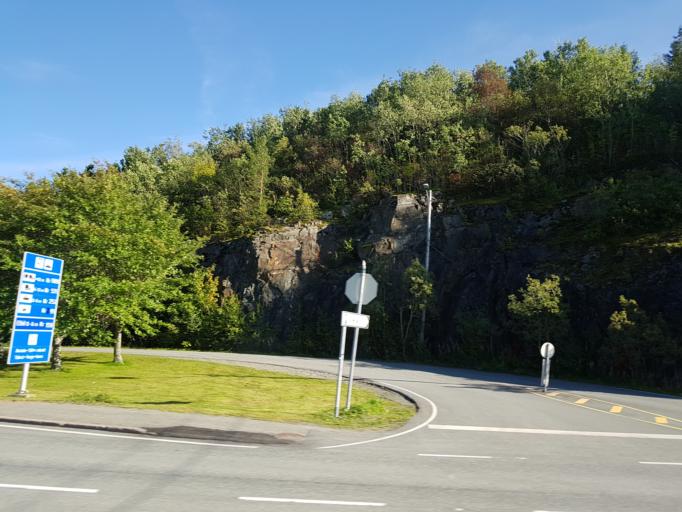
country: NO
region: Sor-Trondelag
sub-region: Skaun
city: Borsa
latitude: 63.4492
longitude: 10.1943
